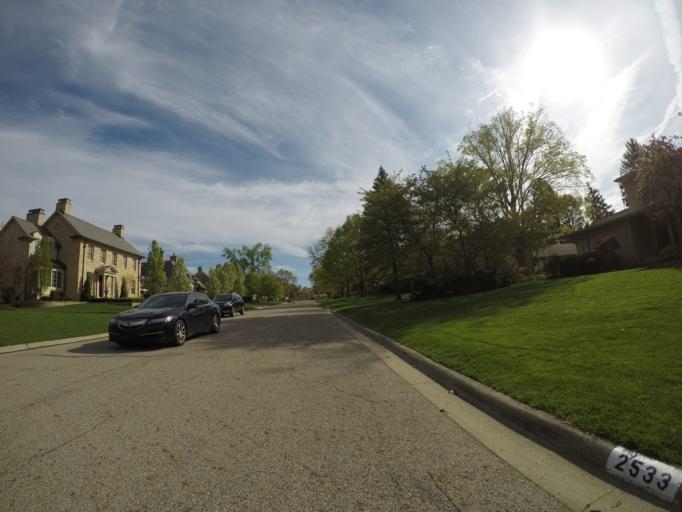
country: US
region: Ohio
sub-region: Franklin County
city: Upper Arlington
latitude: 40.0082
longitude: -83.0787
